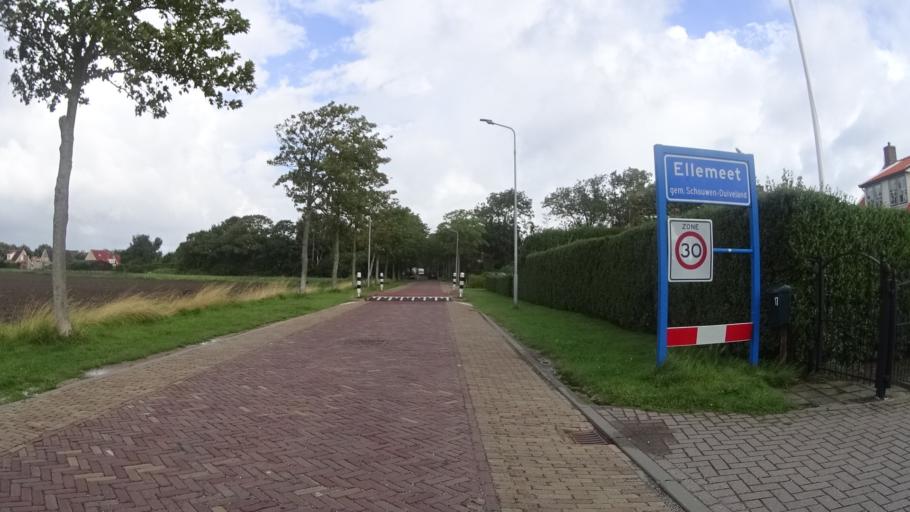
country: NL
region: Zeeland
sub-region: Schouwen-Duiveland
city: Scharendijke
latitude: 51.7278
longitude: 3.8194
